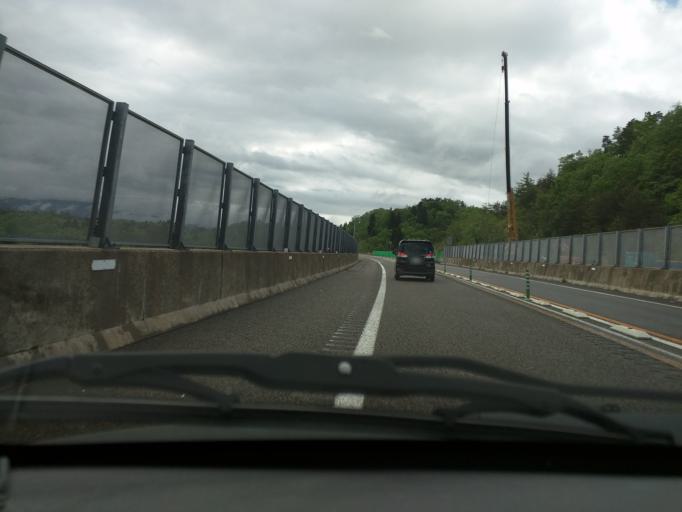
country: JP
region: Niigata
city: Joetsu
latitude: 37.1219
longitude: 138.2135
